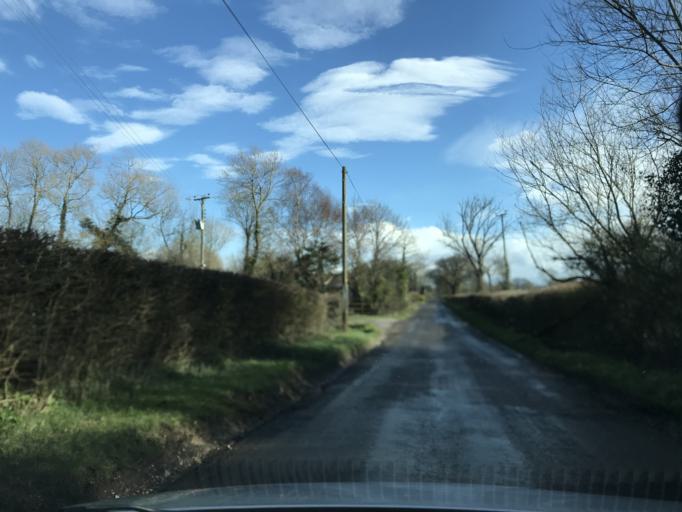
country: GB
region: England
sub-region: Somerset
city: Chard
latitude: 50.9460
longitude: -3.0023
